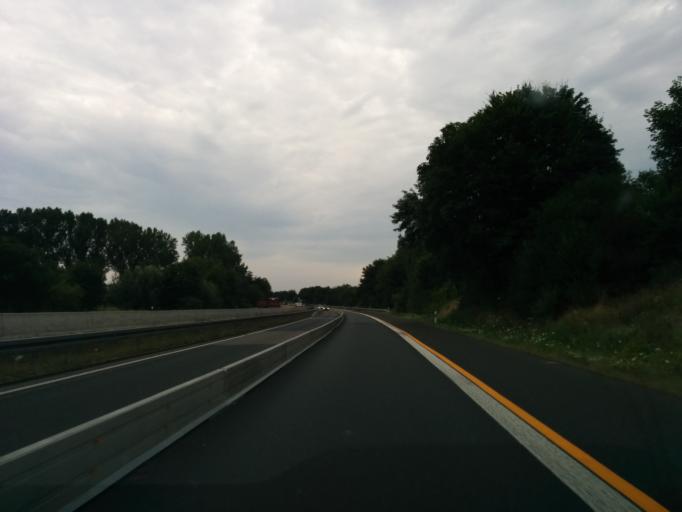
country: DE
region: Hesse
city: Fritzlar
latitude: 51.1616
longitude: 9.3063
